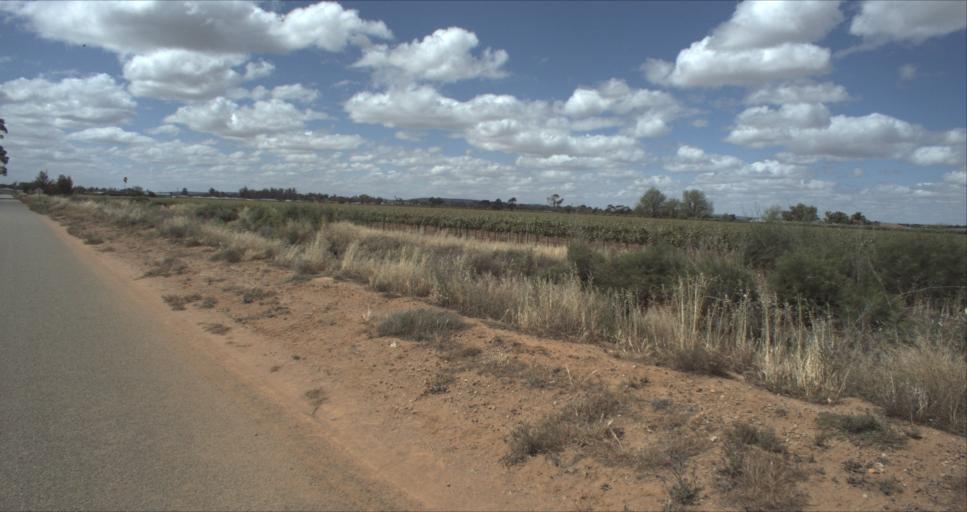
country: AU
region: New South Wales
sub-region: Leeton
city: Leeton
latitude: -34.5777
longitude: 146.3979
